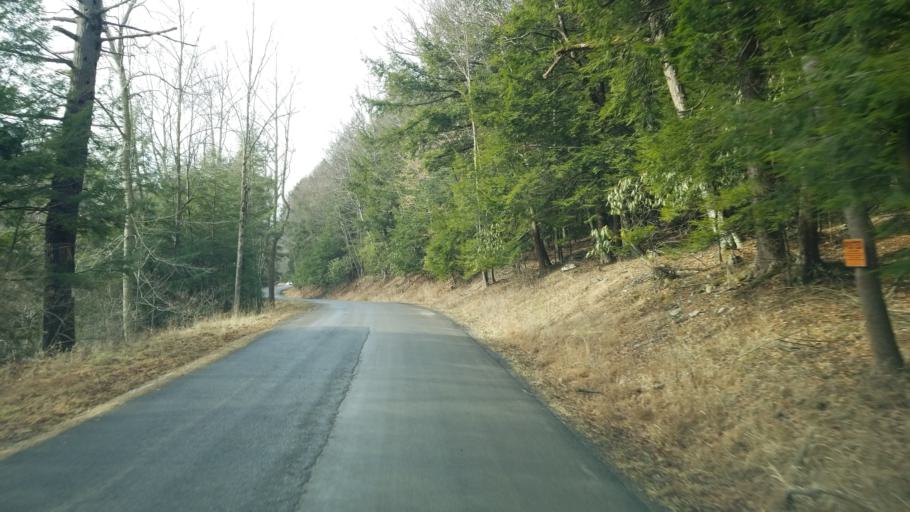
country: US
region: Pennsylvania
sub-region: Indiana County
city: Johnsonburg
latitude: 40.8287
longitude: -78.9594
